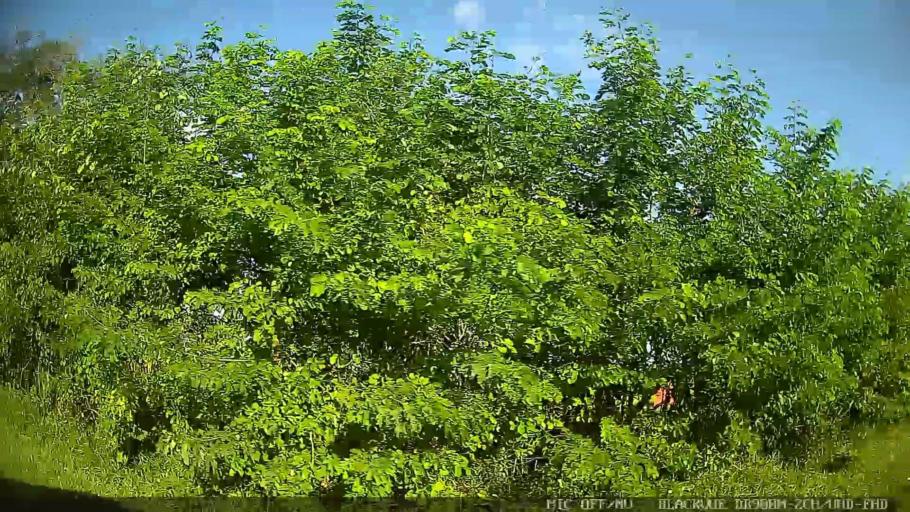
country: BR
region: Sao Paulo
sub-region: Itanhaem
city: Itanhaem
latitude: -24.1521
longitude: -46.8218
